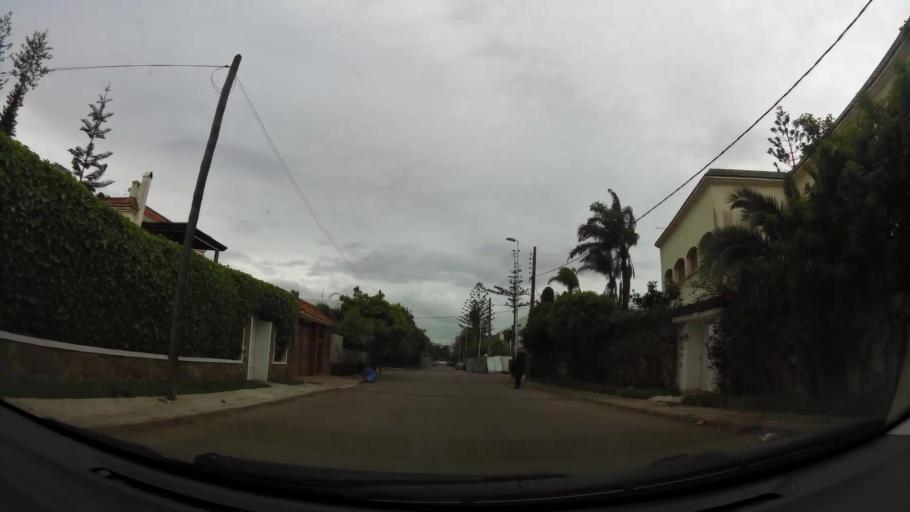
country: MA
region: Grand Casablanca
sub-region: Casablanca
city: Casablanca
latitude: 33.5814
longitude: -7.6556
